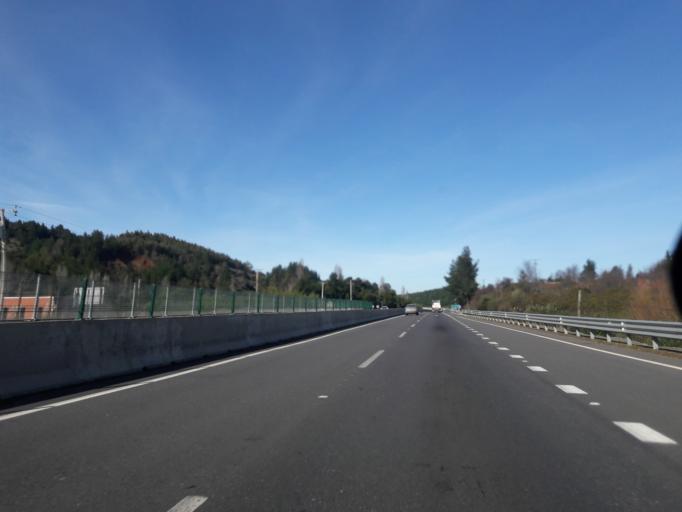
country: CL
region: Biobio
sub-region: Provincia de Biobio
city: Yumbel
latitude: -36.9520
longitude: -72.7480
